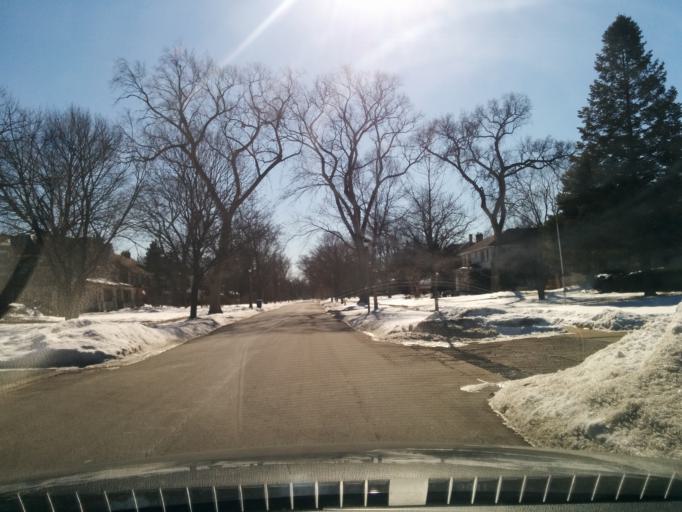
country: US
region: Illinois
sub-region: DuPage County
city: Elmhurst
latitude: 41.8942
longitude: -87.9384
